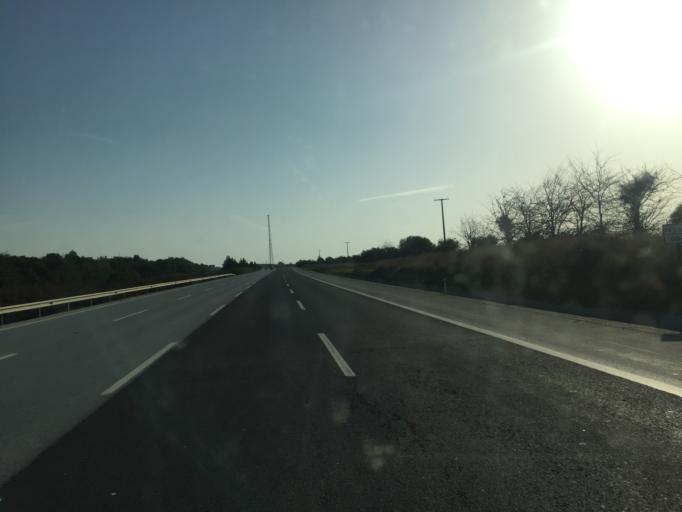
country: TR
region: Mersin
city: Yenice
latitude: 37.0231
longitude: 35.0757
